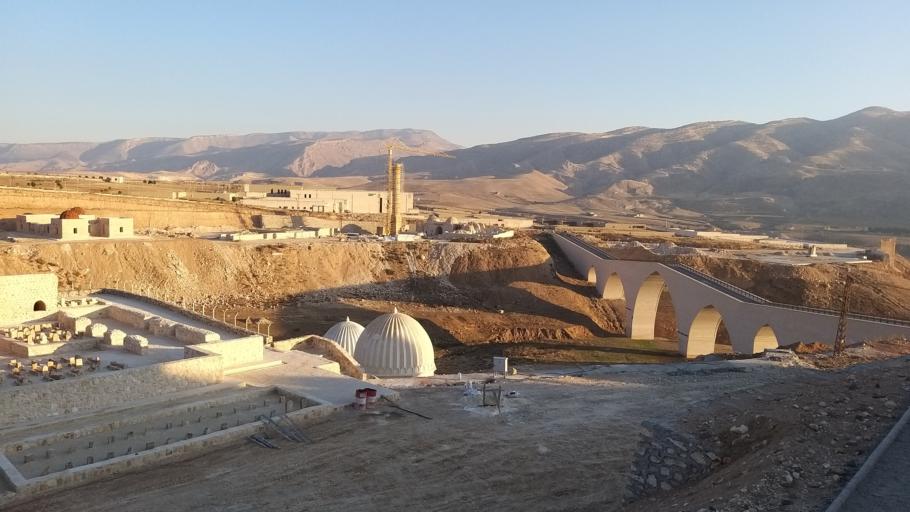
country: TR
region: Batman
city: Hasankeyf
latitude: 37.7294
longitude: 41.4257
